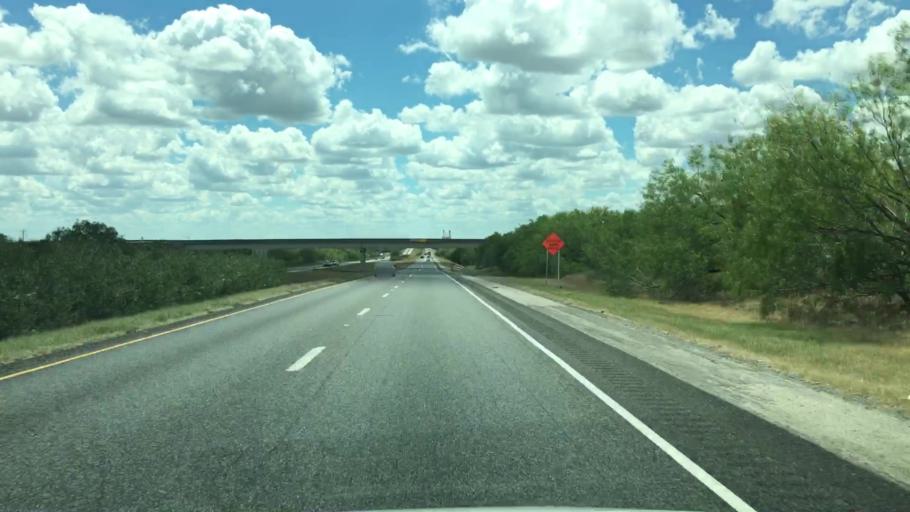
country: US
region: Texas
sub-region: Atascosa County
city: Pleasanton
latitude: 28.9775
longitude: -98.4341
